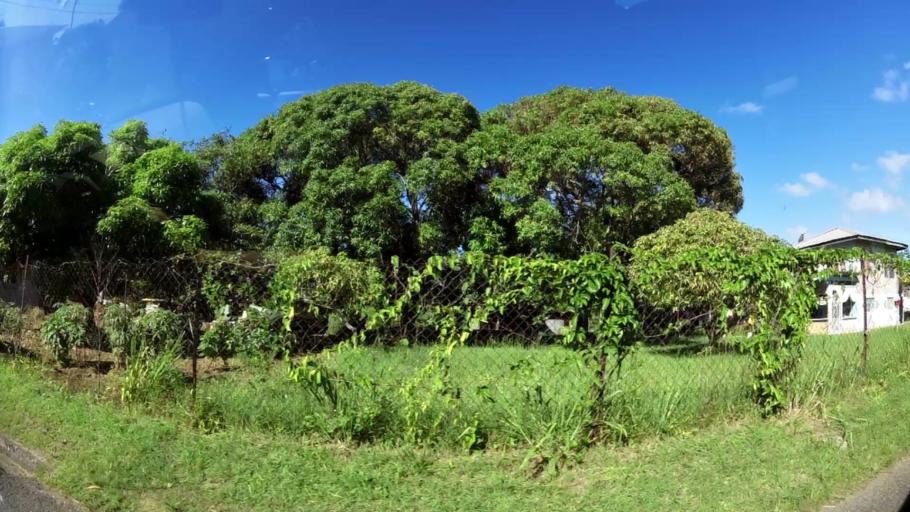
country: TT
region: Tobago
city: Scarborough
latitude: 11.1601
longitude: -60.8067
